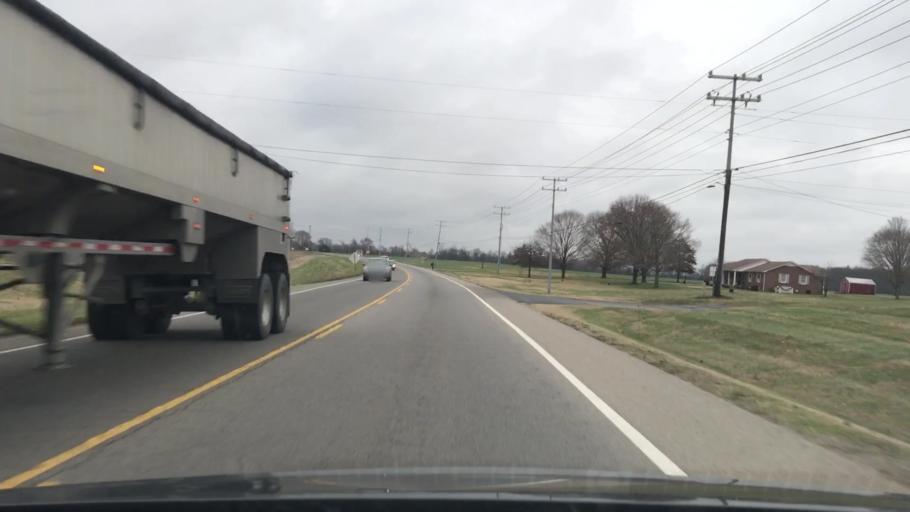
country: US
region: Kentucky
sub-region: Todd County
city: Guthrie
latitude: 36.6111
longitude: -87.2502
